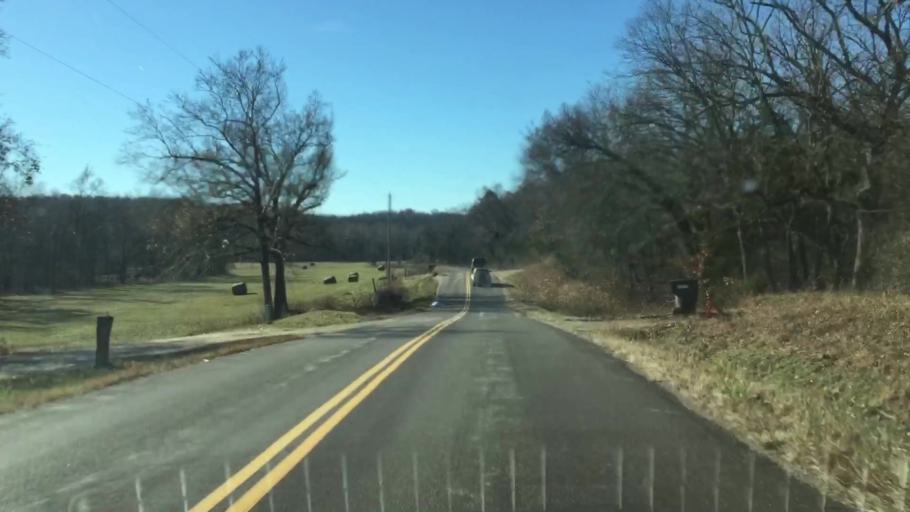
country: US
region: Missouri
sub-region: Miller County
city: Eldon
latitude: 38.3451
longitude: -92.7064
